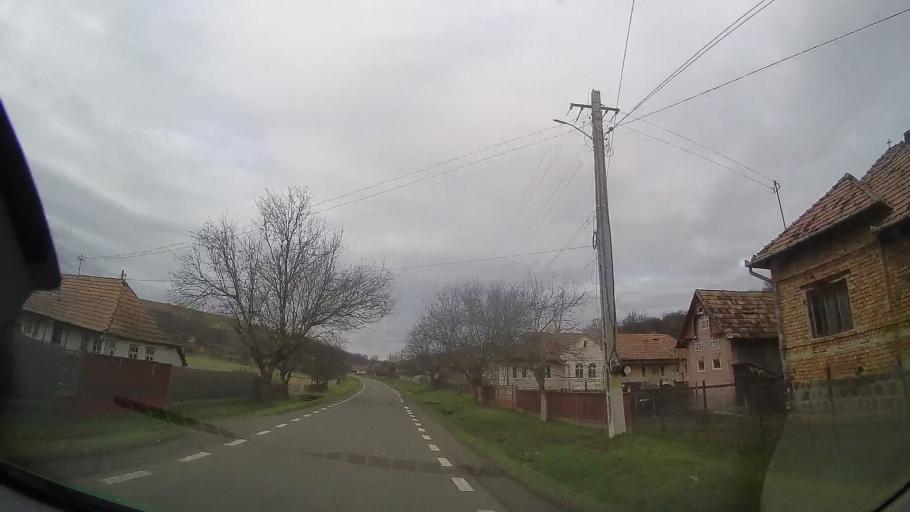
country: RO
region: Mures
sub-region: Comuna Cozma
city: Cozma
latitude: 46.8033
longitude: 24.5323
